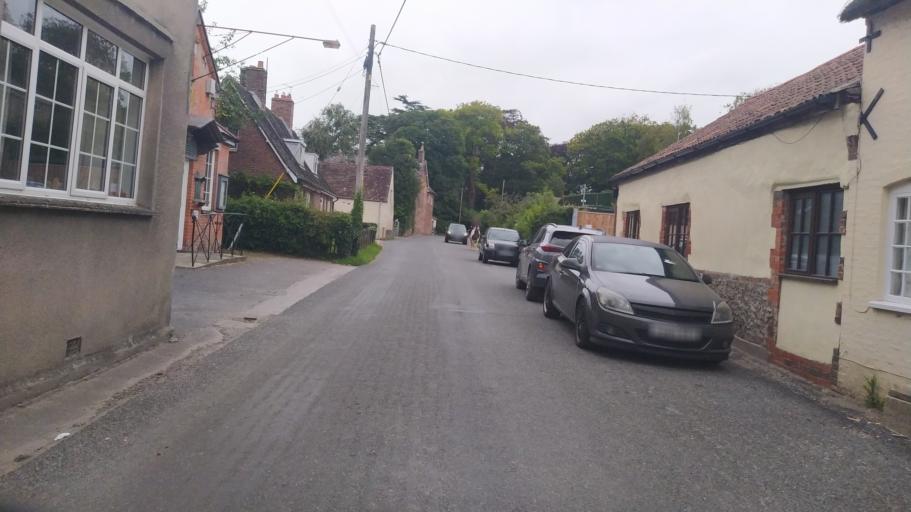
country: GB
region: England
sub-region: Dorset
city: Dorchester
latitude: 50.7971
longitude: -2.4201
